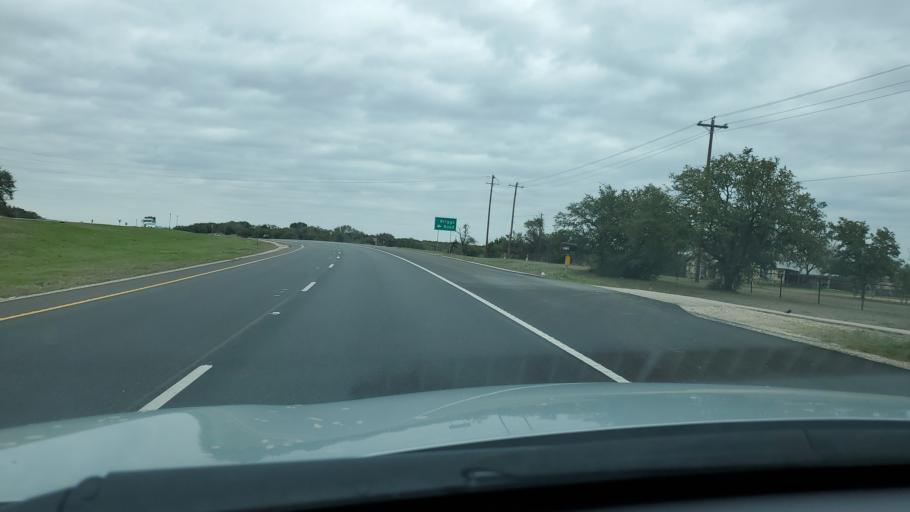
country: US
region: Texas
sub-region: Williamson County
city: Florence
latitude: 30.9437
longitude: -97.7847
